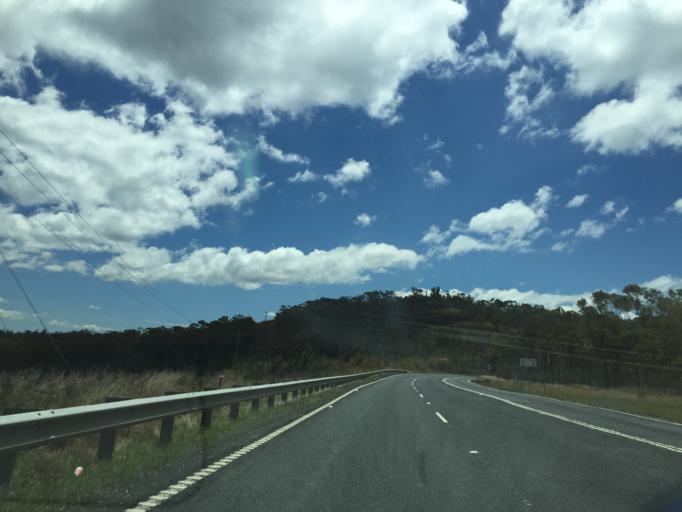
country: AU
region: New South Wales
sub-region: Blue Mountains Municipality
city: Blackheath
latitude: -33.5233
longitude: 150.3063
